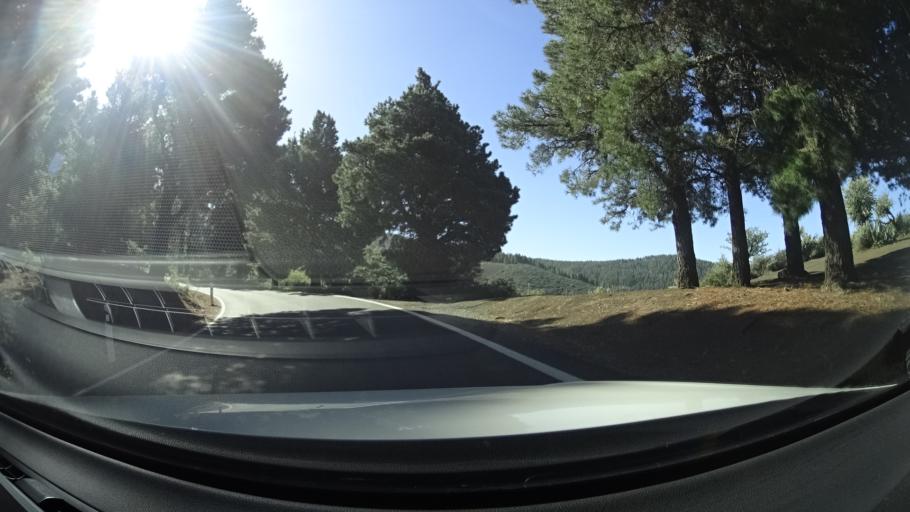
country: ES
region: Canary Islands
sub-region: Provincia de Las Palmas
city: Artenara
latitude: 28.0308
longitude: -15.6212
